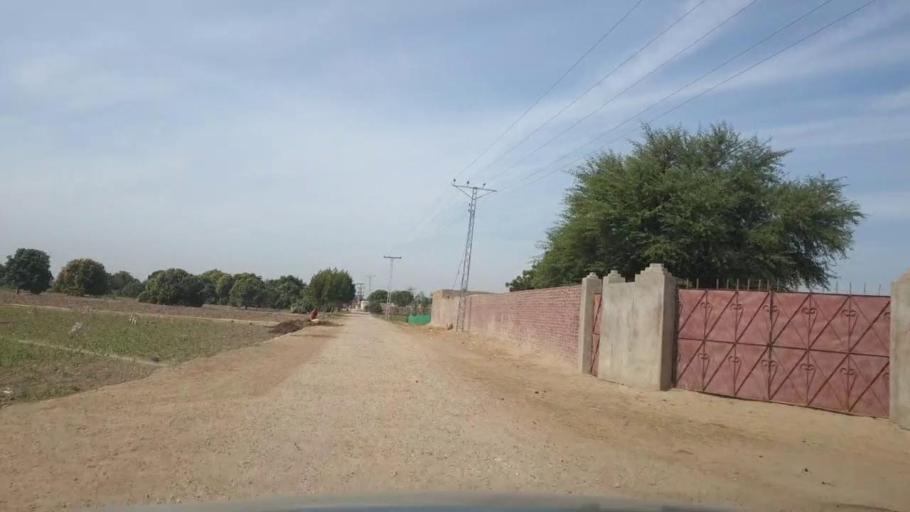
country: PK
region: Sindh
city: Kunri
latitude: 25.1278
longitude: 69.5938
